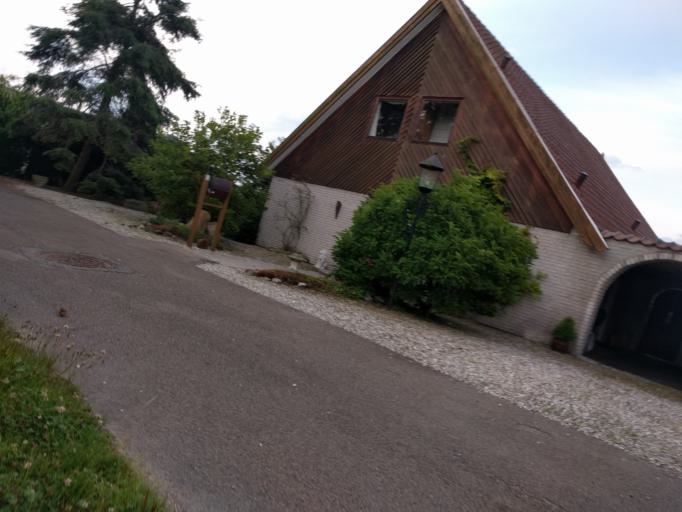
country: DK
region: South Denmark
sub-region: Kerteminde Kommune
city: Munkebo
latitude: 55.4635
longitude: 10.5848
